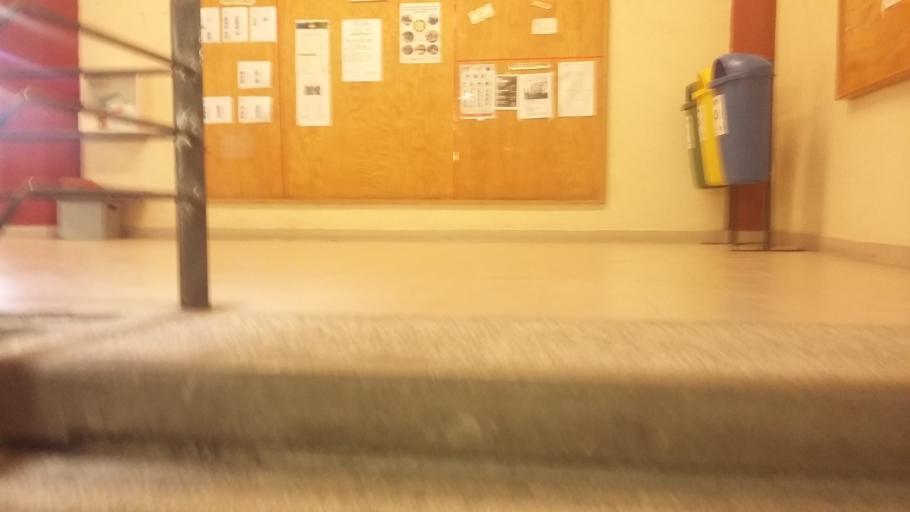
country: MX
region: Mexico
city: Los Reyes La Paz
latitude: 19.3578
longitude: -98.9999
